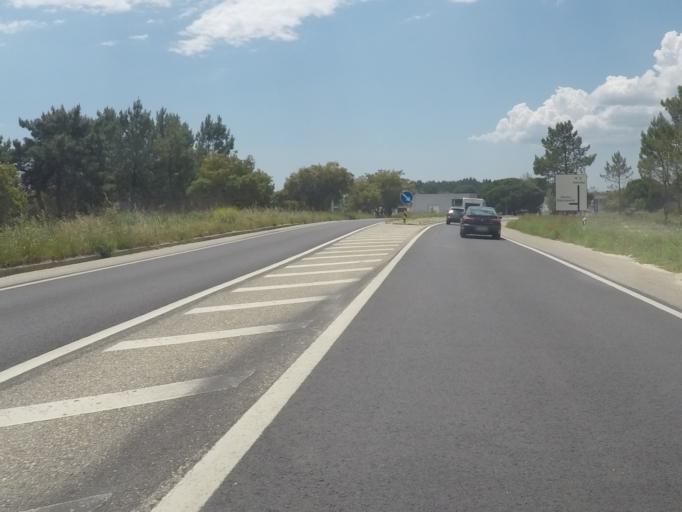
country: PT
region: Setubal
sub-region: Setubal
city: Setubal
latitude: 38.5449
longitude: -8.8238
